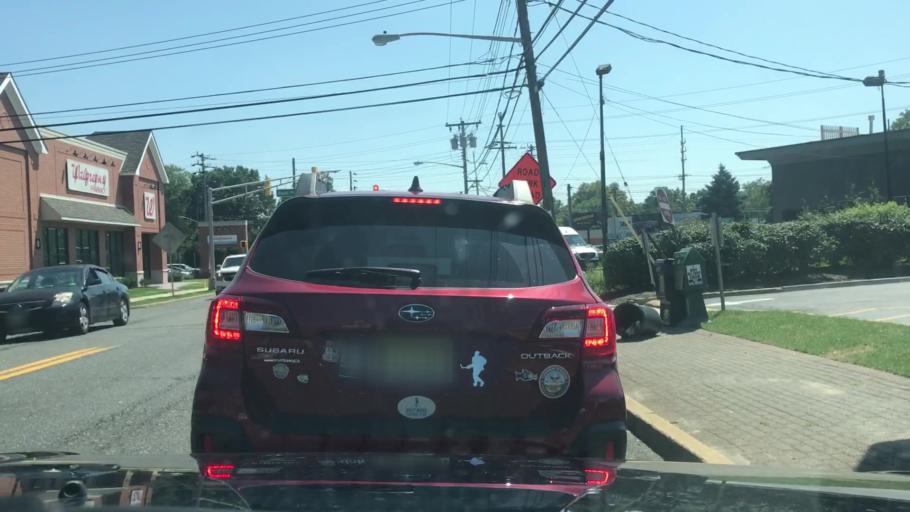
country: US
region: New Jersey
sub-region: Monmouth County
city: Red Bank
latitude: 40.3395
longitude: -74.0639
